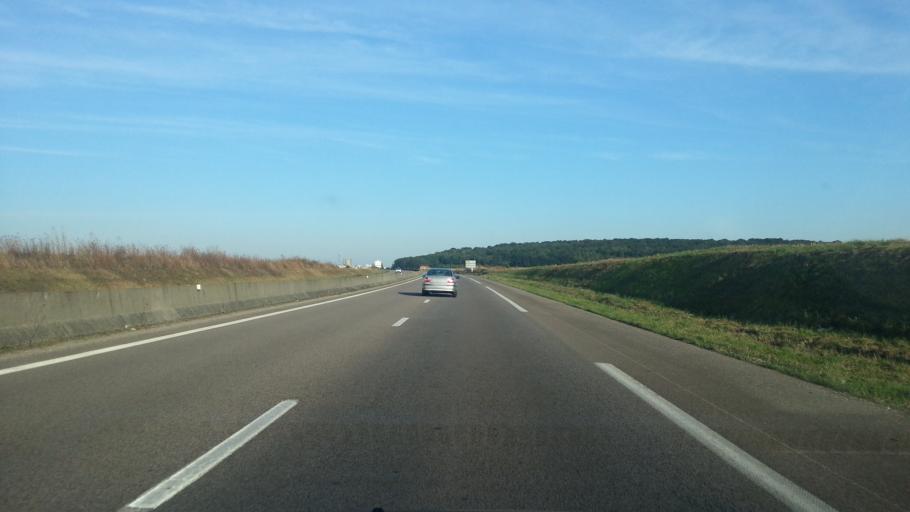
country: FR
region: Picardie
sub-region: Departement de l'Oise
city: Bailleul-sur-Therain
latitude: 49.4120
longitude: 2.1976
